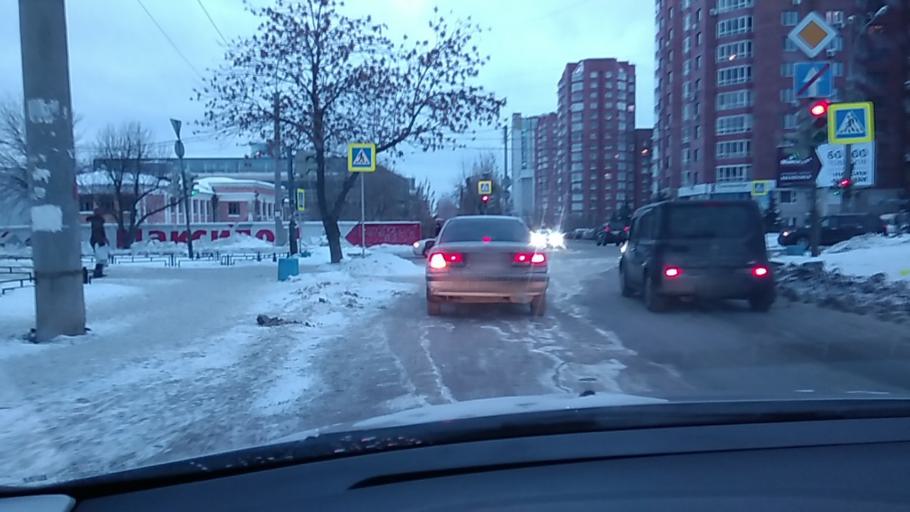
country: RU
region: Sverdlovsk
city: Yekaterinburg
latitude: 56.8224
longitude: 60.6277
